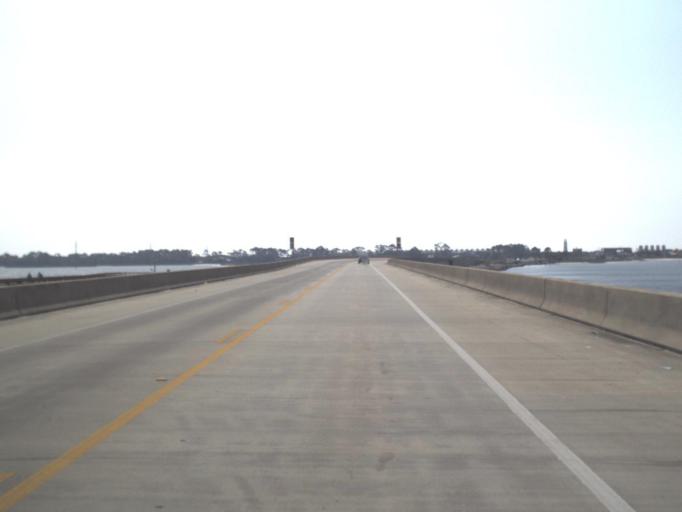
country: US
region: Florida
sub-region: Franklin County
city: Eastpoint
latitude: 29.6737
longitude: -84.8699
